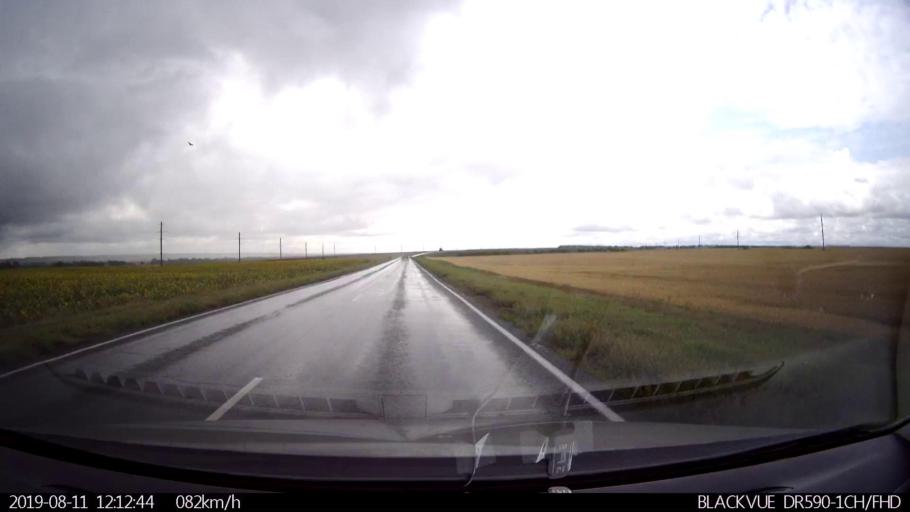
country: RU
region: Ulyanovsk
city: Silikatnyy
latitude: 53.9692
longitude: 47.9952
